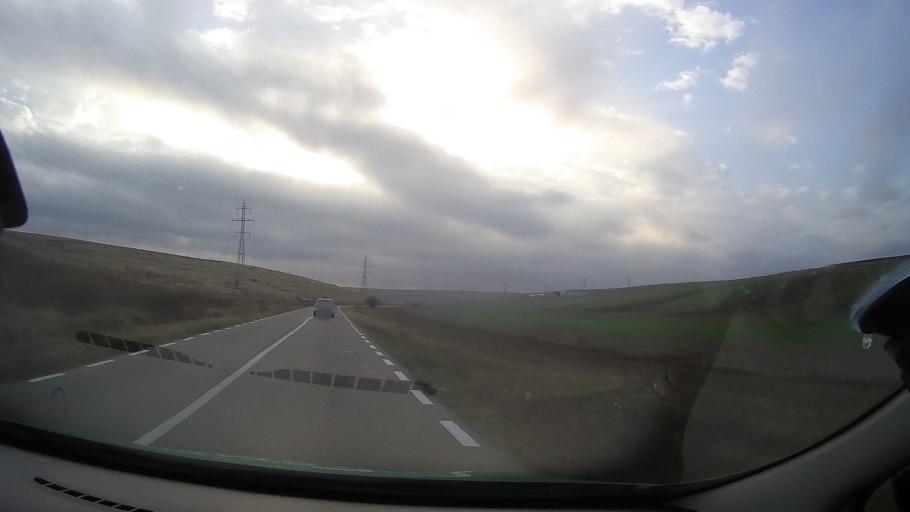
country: RO
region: Constanta
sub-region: Comuna Pestera
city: Pestera
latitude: 44.2027
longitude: 28.1450
